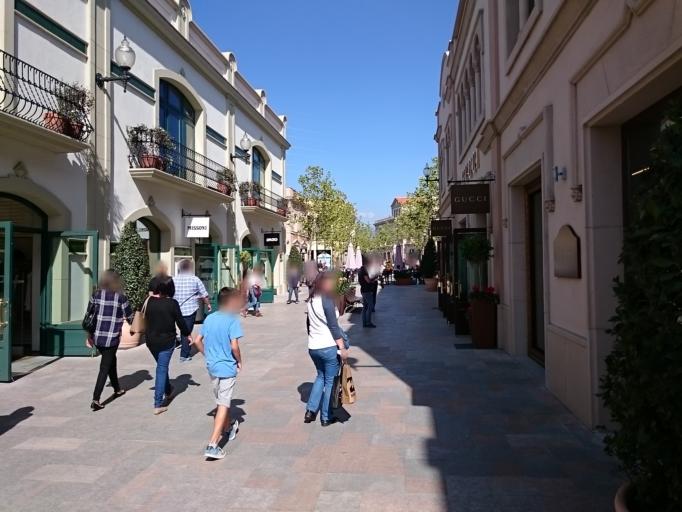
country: ES
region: Catalonia
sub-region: Provincia de Barcelona
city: Cardedeu
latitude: 41.6127
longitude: 2.3448
